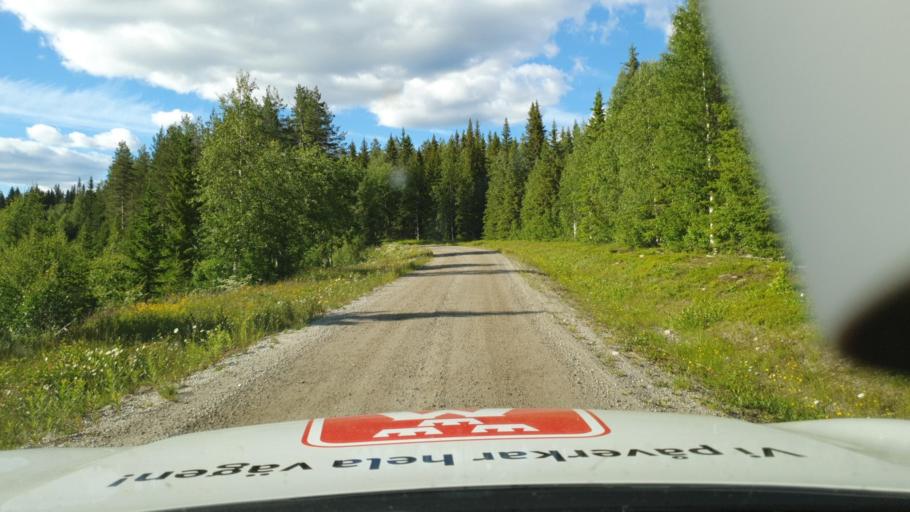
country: SE
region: Vaesterbotten
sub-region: Lycksele Kommun
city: Lycksele
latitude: 64.4071
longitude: 18.2913
